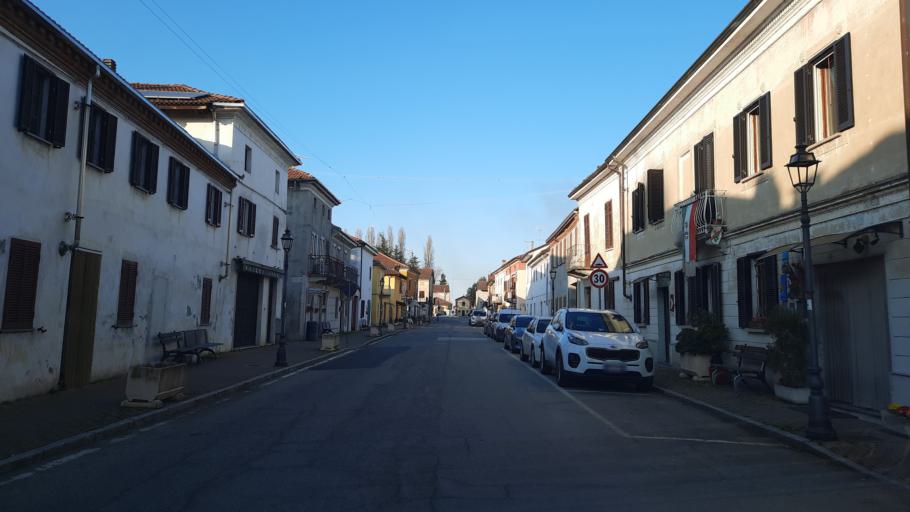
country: IT
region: Piedmont
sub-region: Provincia di Vercelli
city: Costanzana
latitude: 45.2364
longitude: 8.3703
